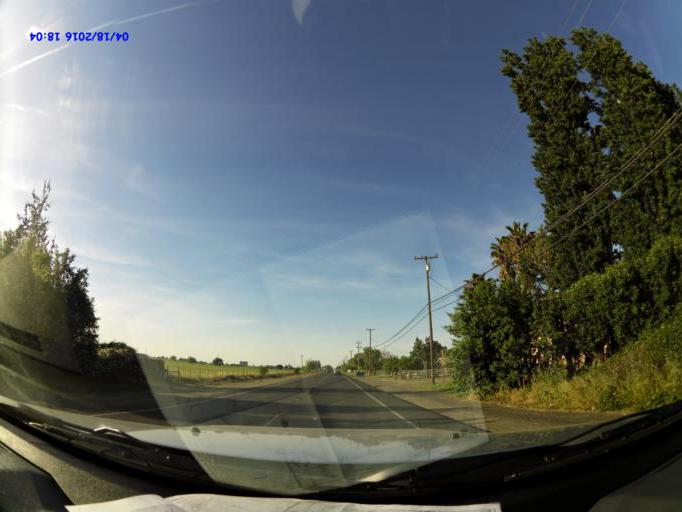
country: US
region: California
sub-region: San Joaquin County
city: Escalon
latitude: 37.8109
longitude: -120.9971
